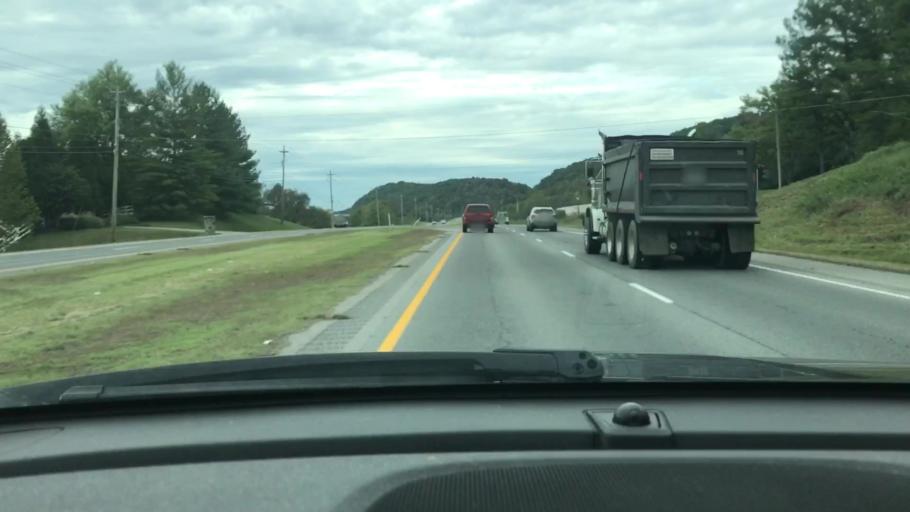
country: US
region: Tennessee
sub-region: Cheatham County
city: Ashland City
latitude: 36.2246
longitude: -87.0070
